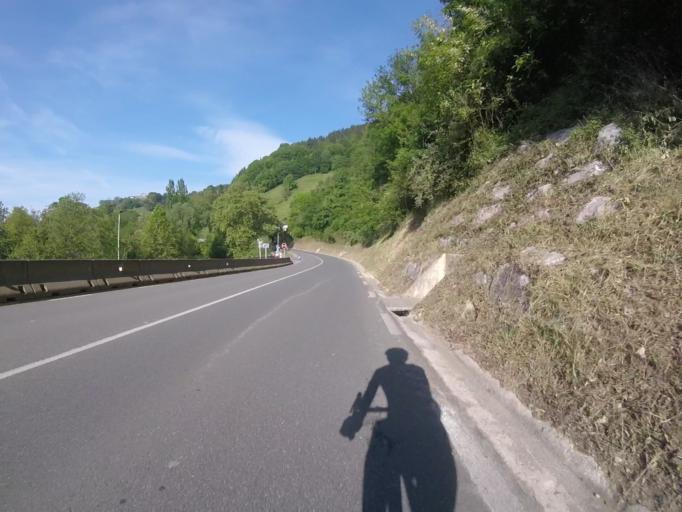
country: ES
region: Basque Country
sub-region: Provincia de Guipuzcoa
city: Arama
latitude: 43.0642
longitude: -2.1712
